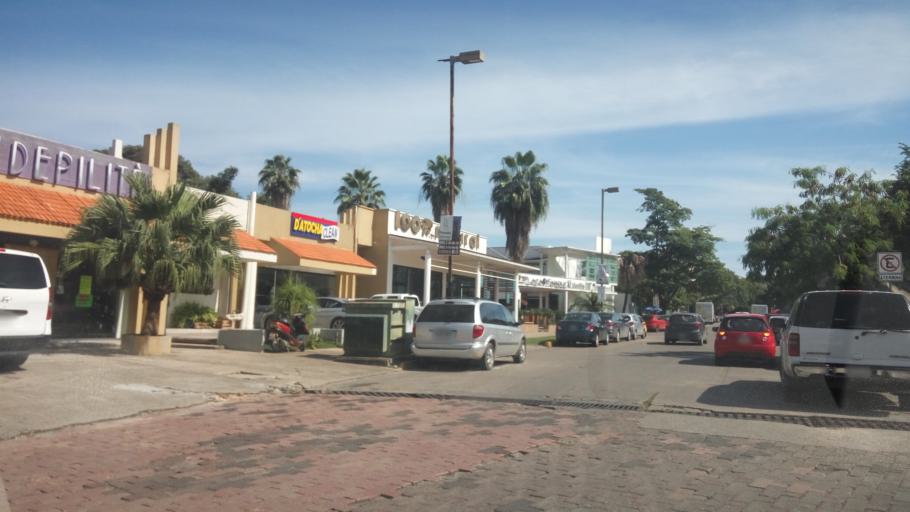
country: MX
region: Tabasco
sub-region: Nacajuca
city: Bosque de Saloya
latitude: 18.0016
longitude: -92.9443
